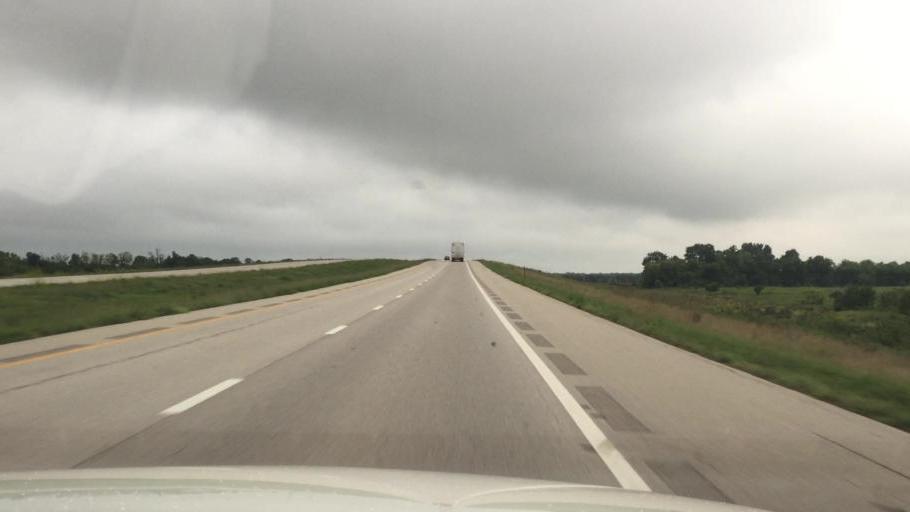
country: US
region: Kansas
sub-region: Montgomery County
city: Coffeyville
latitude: 37.0902
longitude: -95.5898
